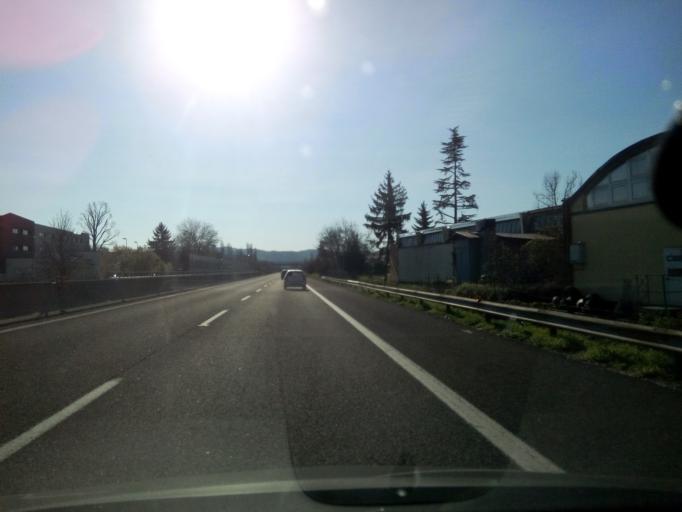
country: IT
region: Emilia-Romagna
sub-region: Provincia di Bologna
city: Riale
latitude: 44.4956
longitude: 11.2332
